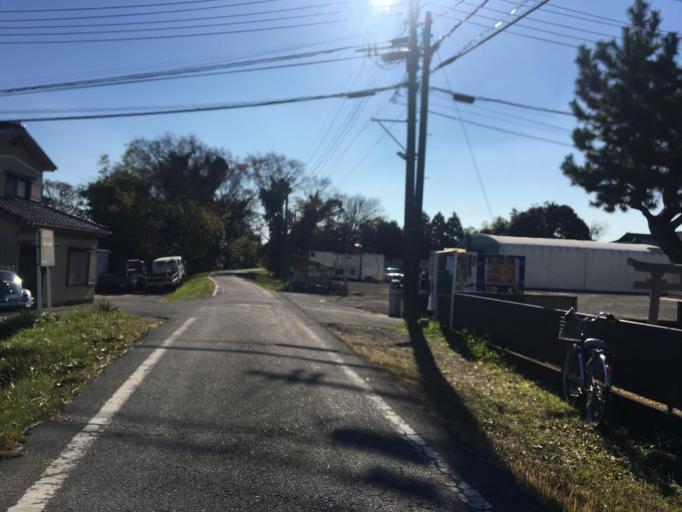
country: JP
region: Saitama
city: Yashio-shi
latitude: 35.8396
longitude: 139.8406
